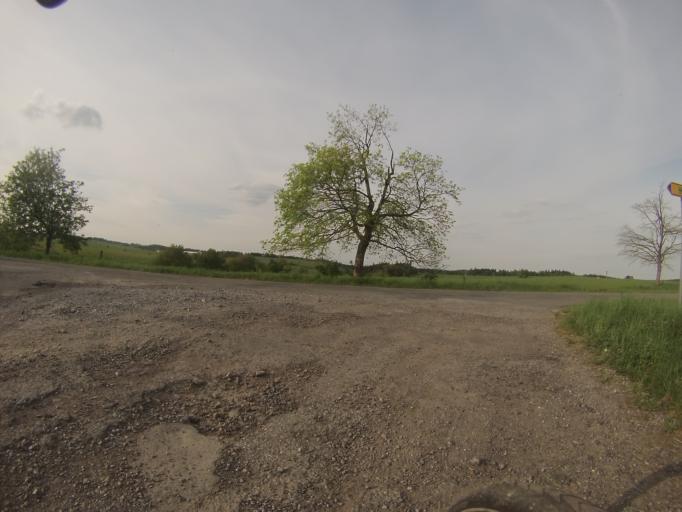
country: CZ
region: Olomoucky
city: Protivanov
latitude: 49.4595
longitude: 16.8727
